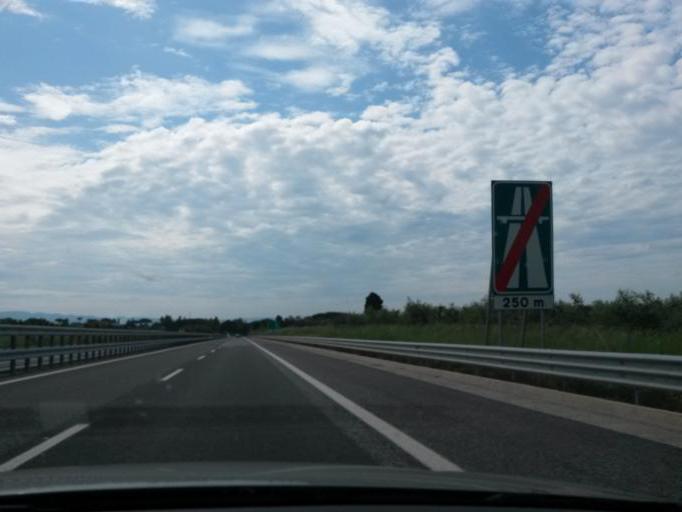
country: IT
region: Tuscany
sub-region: Provincia di Livorno
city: S.P. in Palazzi
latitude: 43.3467
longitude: 10.5171
